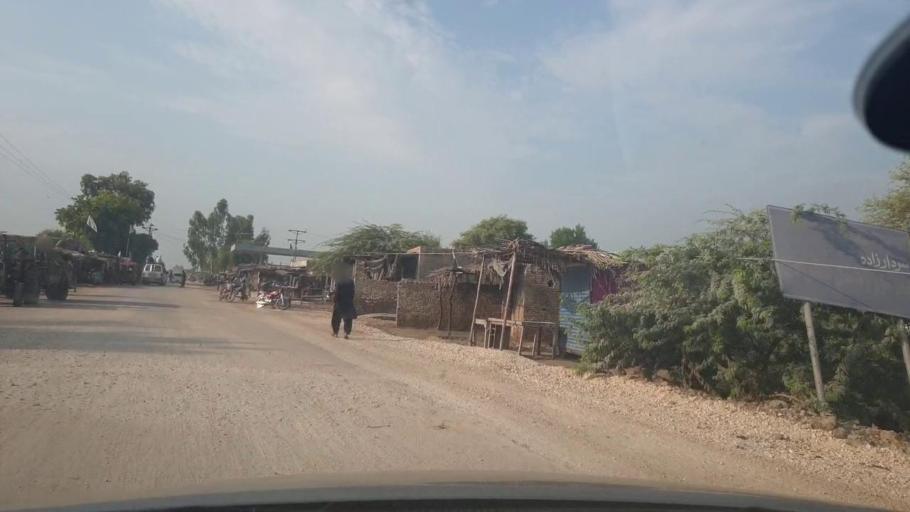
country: PK
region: Sindh
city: Jacobabad
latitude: 28.2154
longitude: 68.3688
